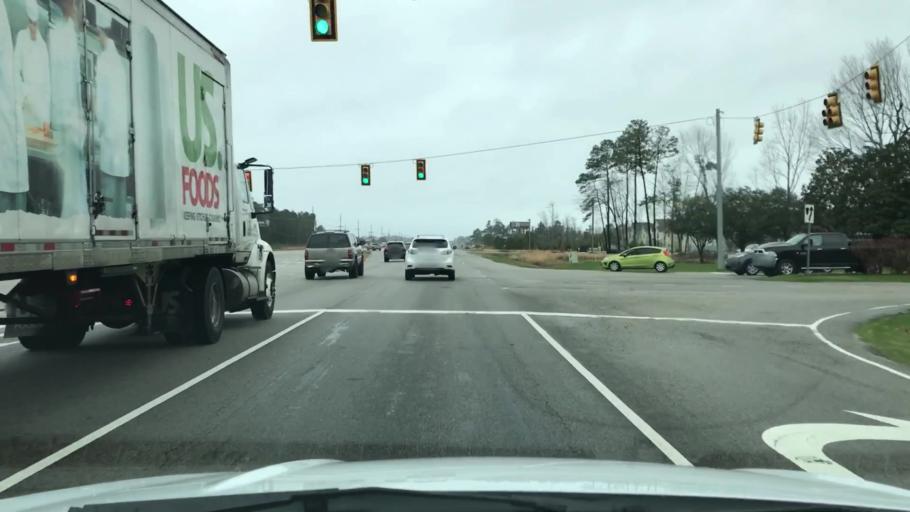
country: US
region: South Carolina
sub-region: Horry County
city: Red Hill
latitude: 33.7823
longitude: -78.9891
